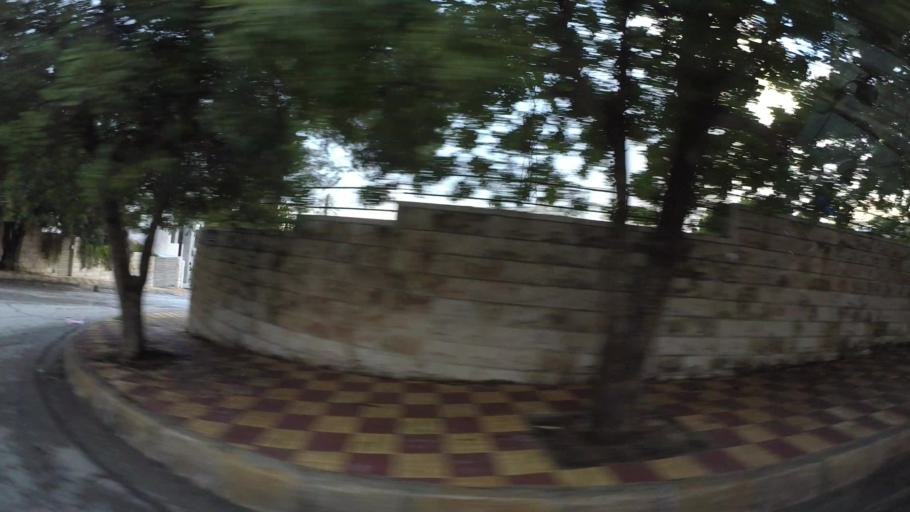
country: JO
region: Amman
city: Amman
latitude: 31.9604
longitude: 35.8871
